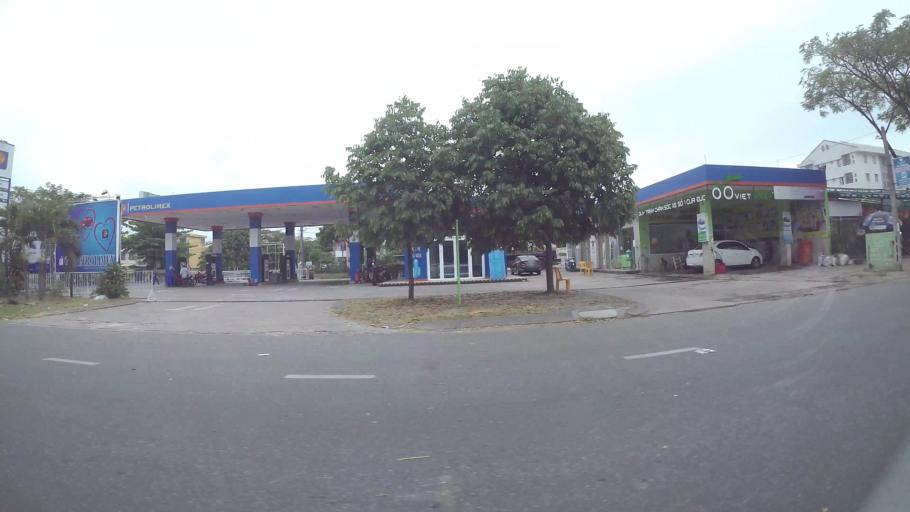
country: VN
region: Da Nang
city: Lien Chieu
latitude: 16.0741
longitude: 108.1705
